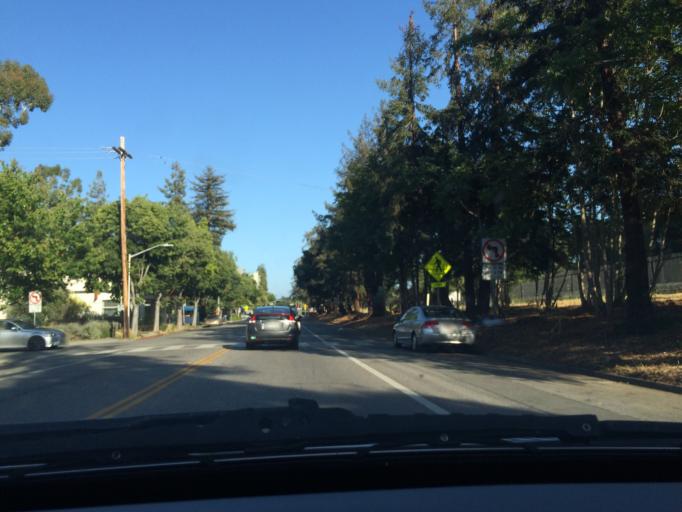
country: US
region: California
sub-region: San Mateo County
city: Menlo Park
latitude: 37.4461
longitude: -122.1682
